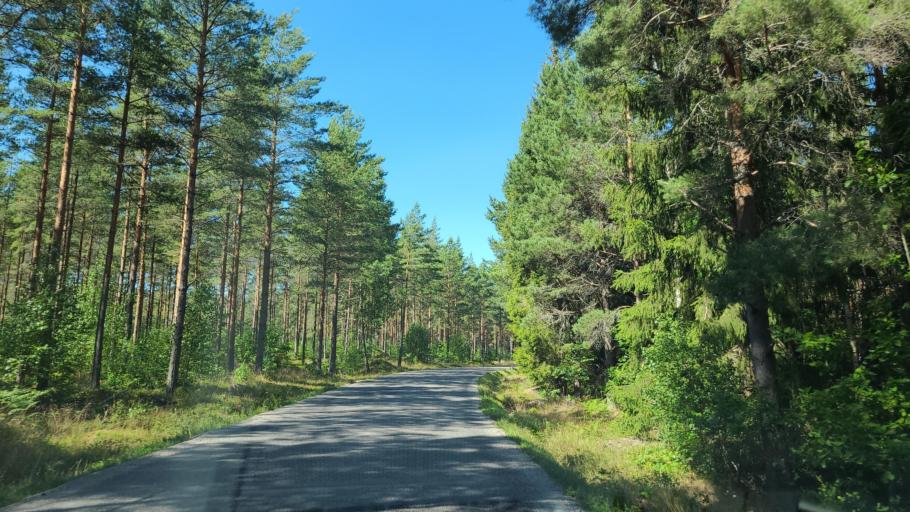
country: SE
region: Kalmar
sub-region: Kalmar Kommun
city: Ljungbyholm
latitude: 56.5709
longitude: 16.0353
